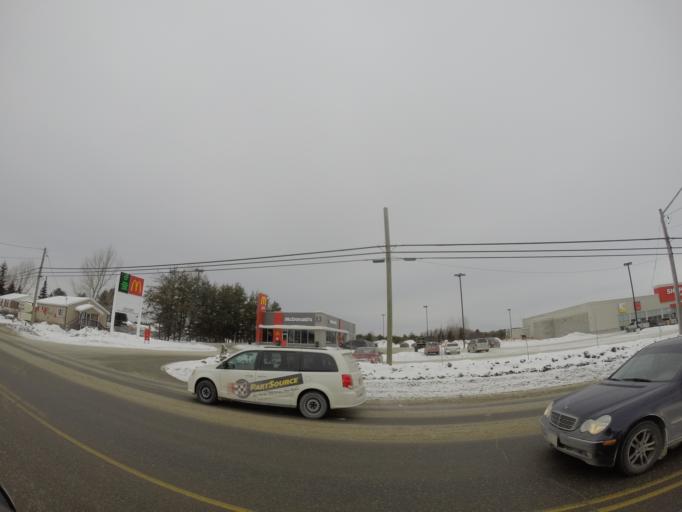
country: CA
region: Ontario
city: Greater Sudbury
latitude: 46.6528
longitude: -80.9889
